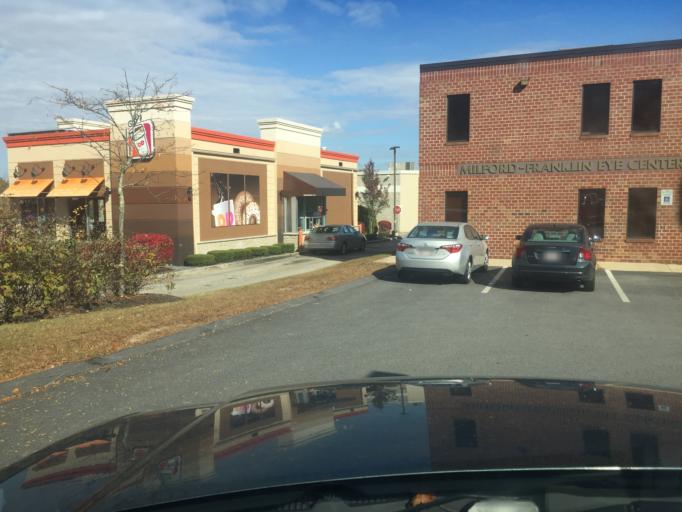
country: US
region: Massachusetts
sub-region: Worcester County
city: Milford
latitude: 42.1245
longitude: -71.5165
